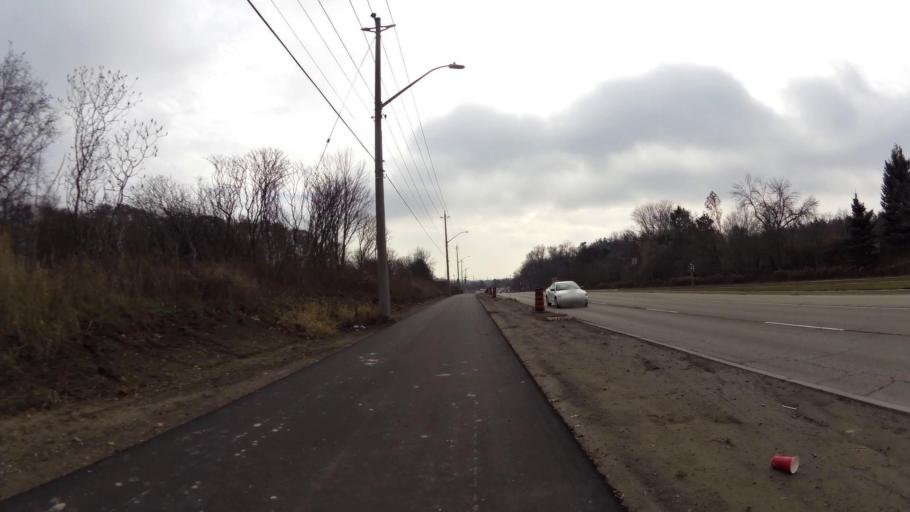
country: CA
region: Ontario
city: Kitchener
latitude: 43.4122
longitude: -80.4633
